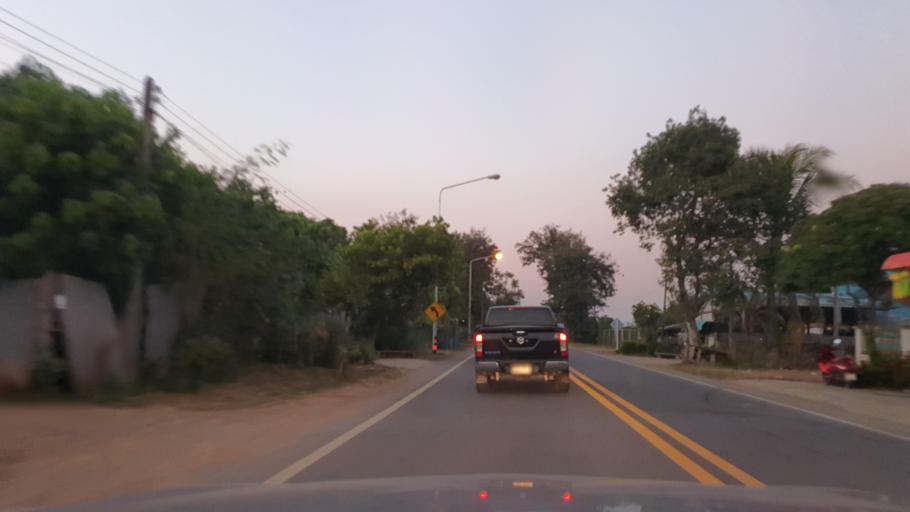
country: TH
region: Phayao
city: Dok Kham Tai
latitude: 19.1463
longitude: 100.0137
